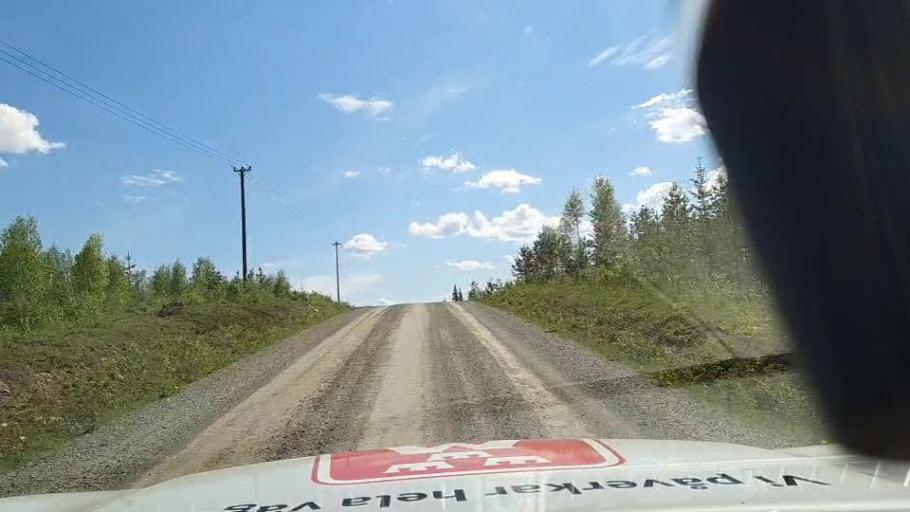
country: SE
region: Jaemtland
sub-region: Stroemsunds Kommun
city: Stroemsund
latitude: 64.4869
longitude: 15.5914
